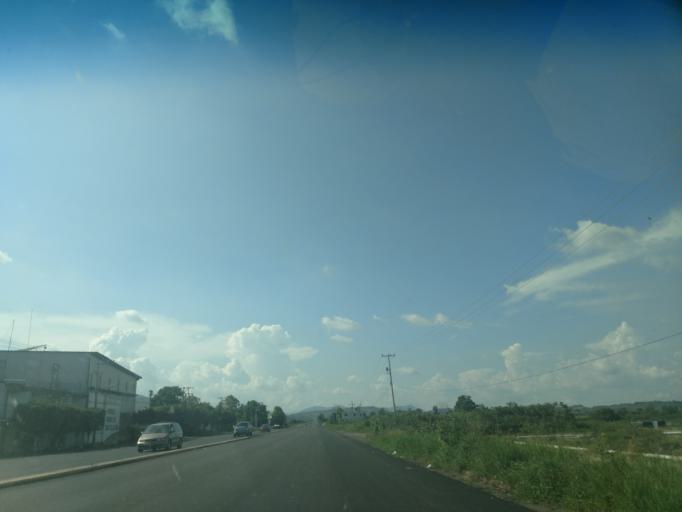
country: MX
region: Jalisco
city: Ahualulco de Mercado
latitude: 20.7095
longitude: -103.9735
